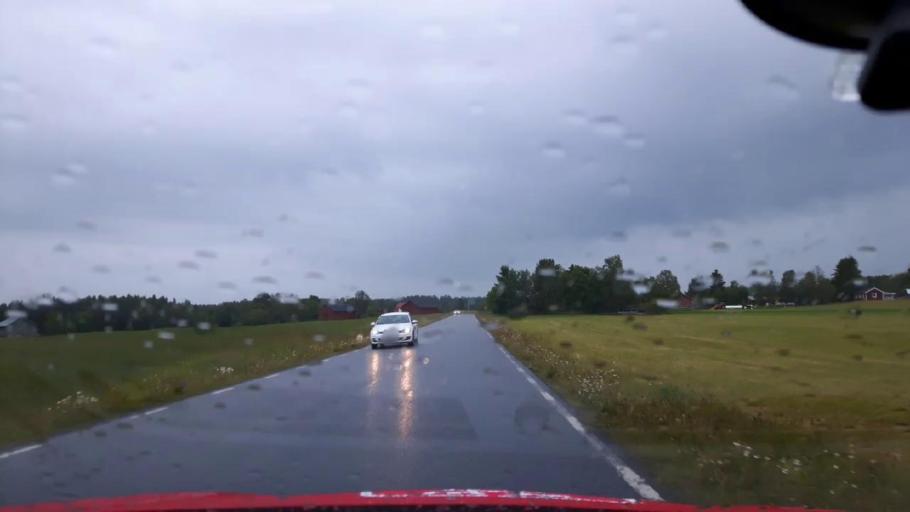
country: SE
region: Jaemtland
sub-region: OEstersunds Kommun
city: Brunflo
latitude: 63.0143
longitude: 14.7339
